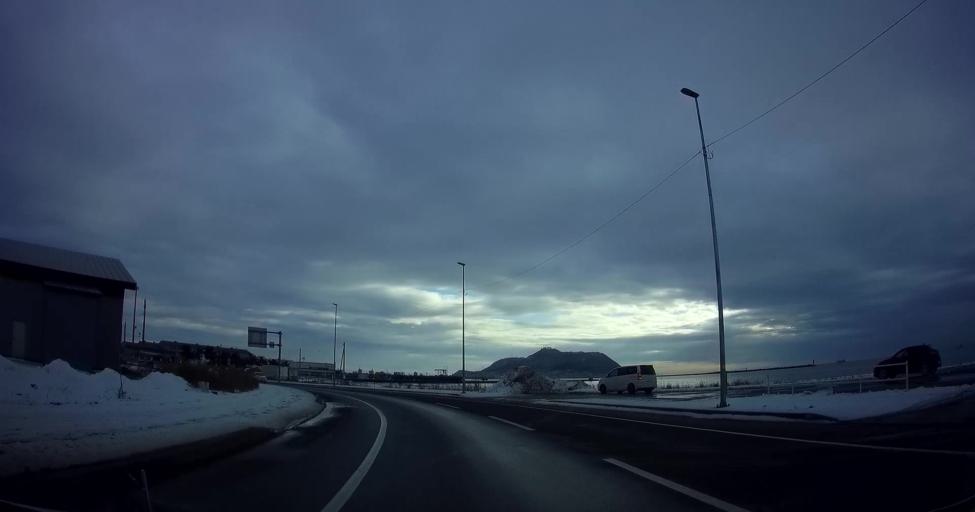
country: JP
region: Hokkaido
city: Hakodate
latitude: 41.8157
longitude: 140.7028
